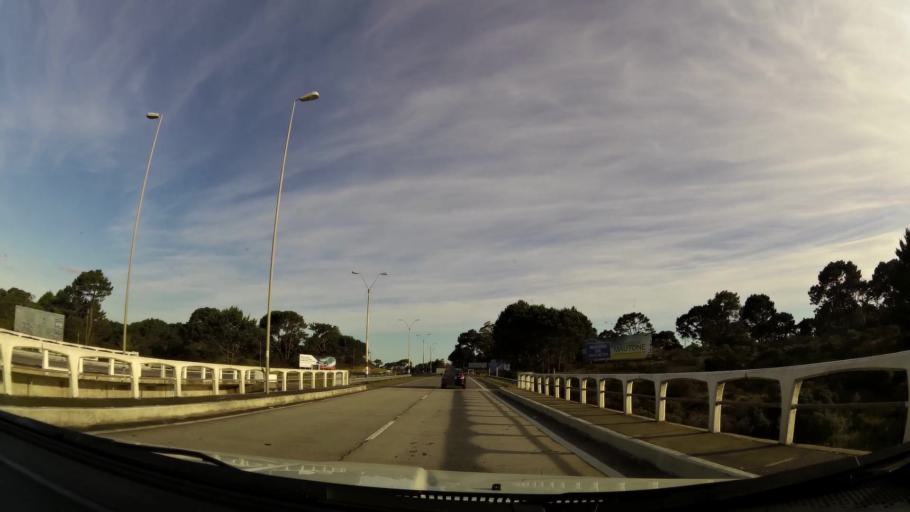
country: UY
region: Maldonado
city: Maldonado
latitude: -34.8699
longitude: -55.0801
